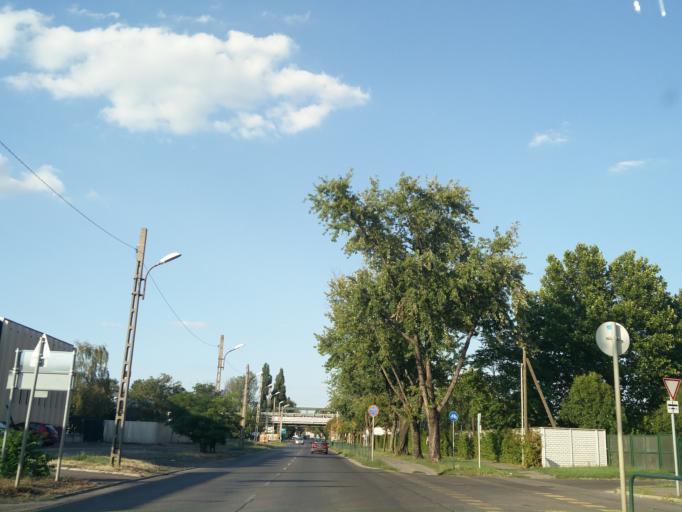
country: HU
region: Budapest
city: Budapest XIX. keruelet
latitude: 47.4698
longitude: 19.1289
